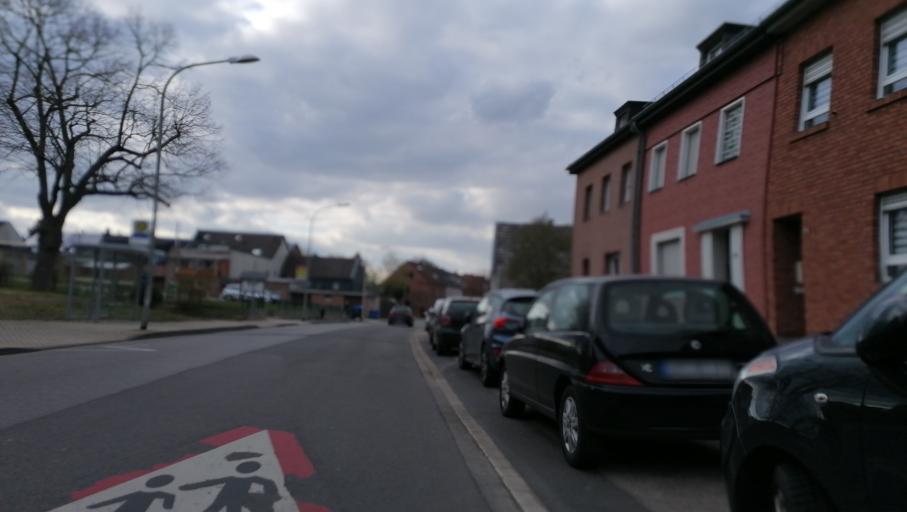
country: DE
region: North Rhine-Westphalia
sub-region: Regierungsbezirk Koln
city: Dueren
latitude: 50.7990
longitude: 6.4339
